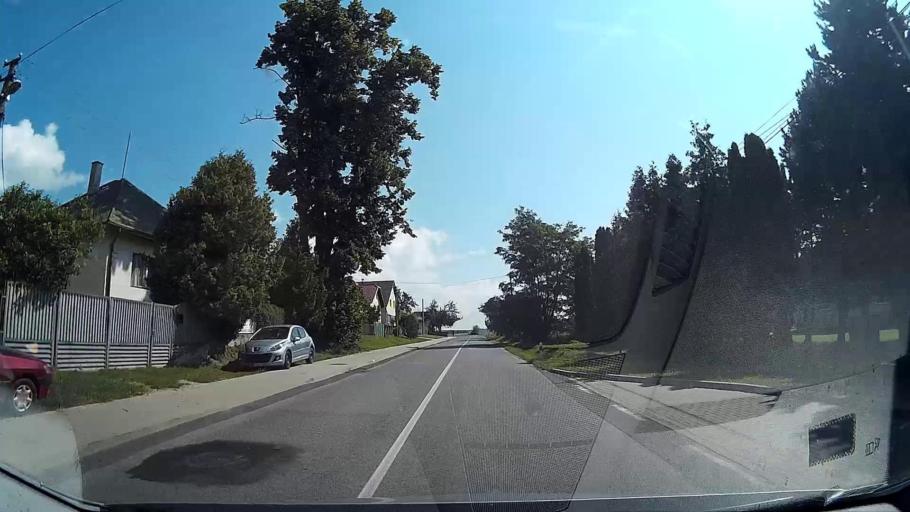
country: SK
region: Presovsky
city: Lubica
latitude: 48.9814
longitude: 20.4192
